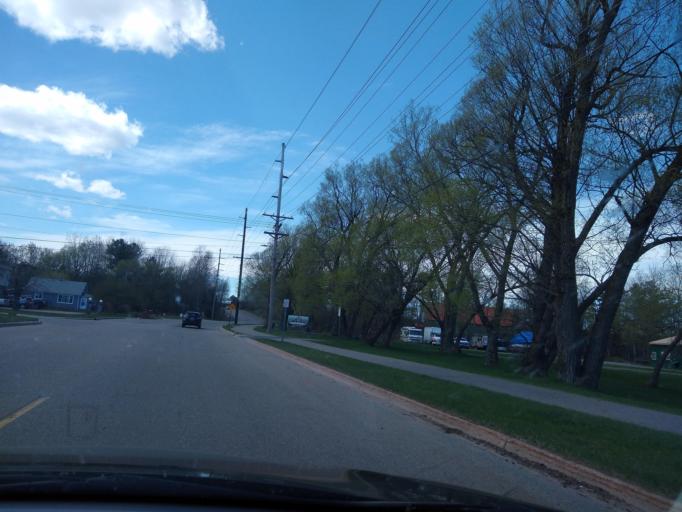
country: US
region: Michigan
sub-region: Marquette County
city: Marquette
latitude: 46.5713
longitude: -87.3983
